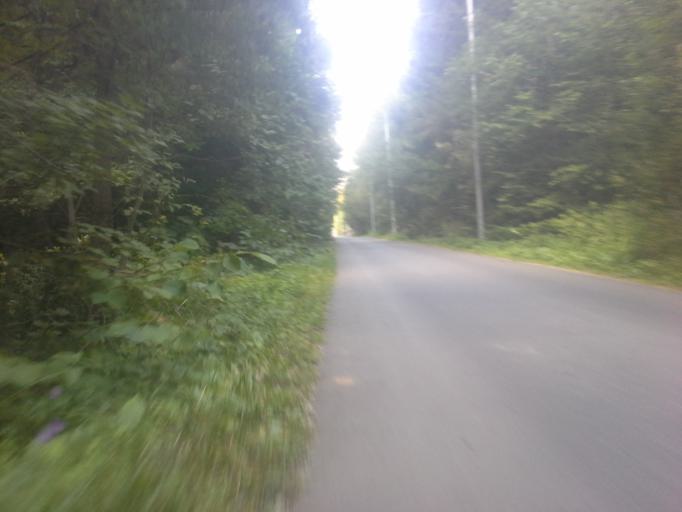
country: RU
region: Moskovskaya
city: Kievskij
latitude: 55.3434
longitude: 36.9484
